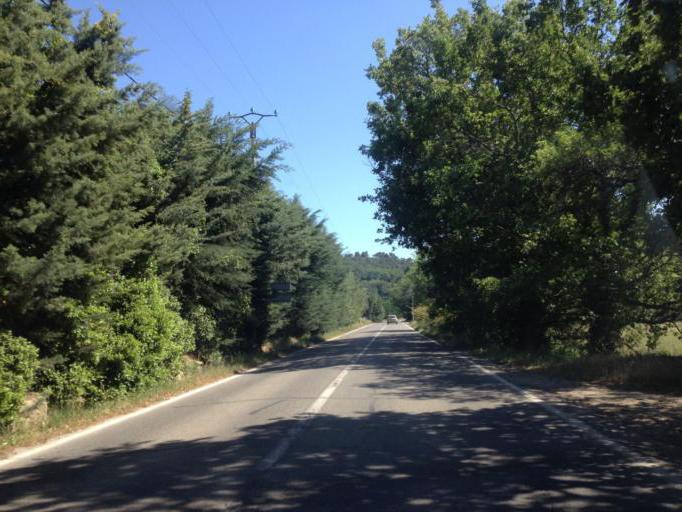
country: FR
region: Provence-Alpes-Cote d'Azur
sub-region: Departement du Vaucluse
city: Lourmarin
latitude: 43.7599
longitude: 5.3650
